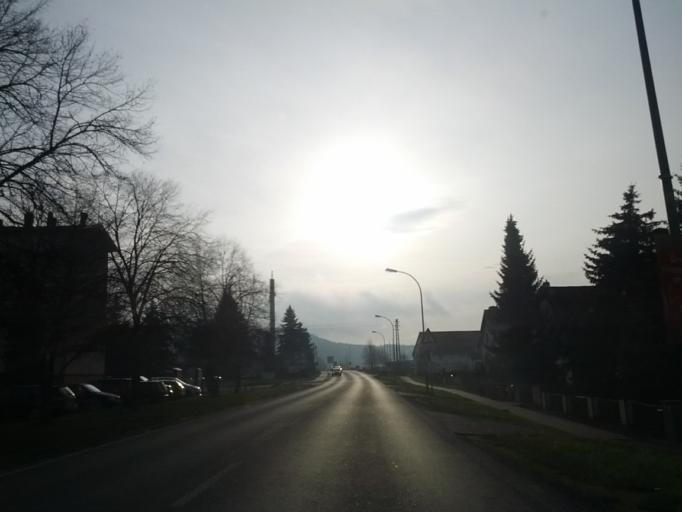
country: DE
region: Thuringia
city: Wasungen
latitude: 50.6586
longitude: 10.3730
